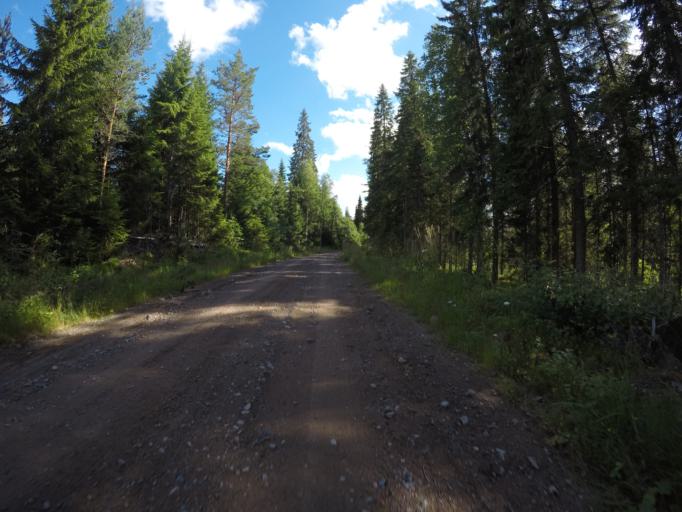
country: SE
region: Dalarna
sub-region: Ludvika Kommun
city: Abborrberget
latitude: 60.0091
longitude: 14.6098
